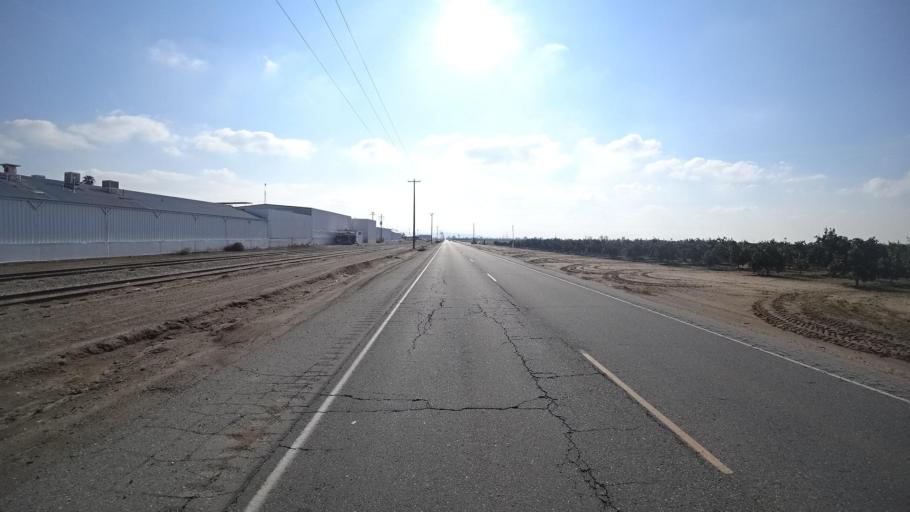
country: US
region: California
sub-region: Kern County
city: Arvin
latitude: 35.2284
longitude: -118.8244
